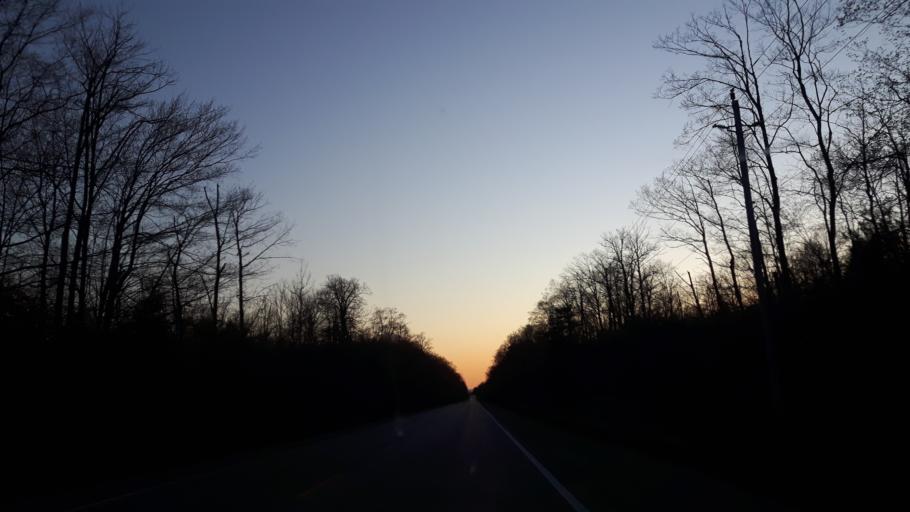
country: CA
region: Ontario
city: Bluewater
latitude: 43.5870
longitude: -81.6698
